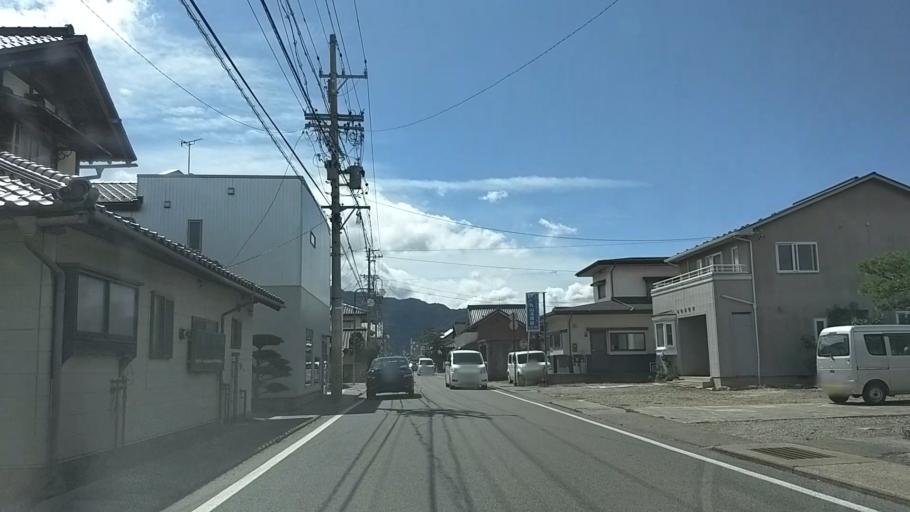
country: JP
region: Nagano
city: Suzaka
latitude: 36.6249
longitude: 138.2576
